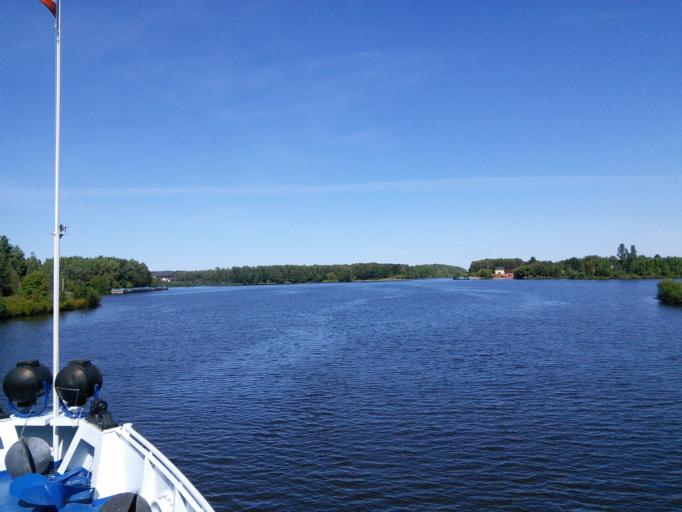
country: RU
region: Moskovskaya
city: Pirogovskiy
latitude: 56.0389
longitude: 37.6676
